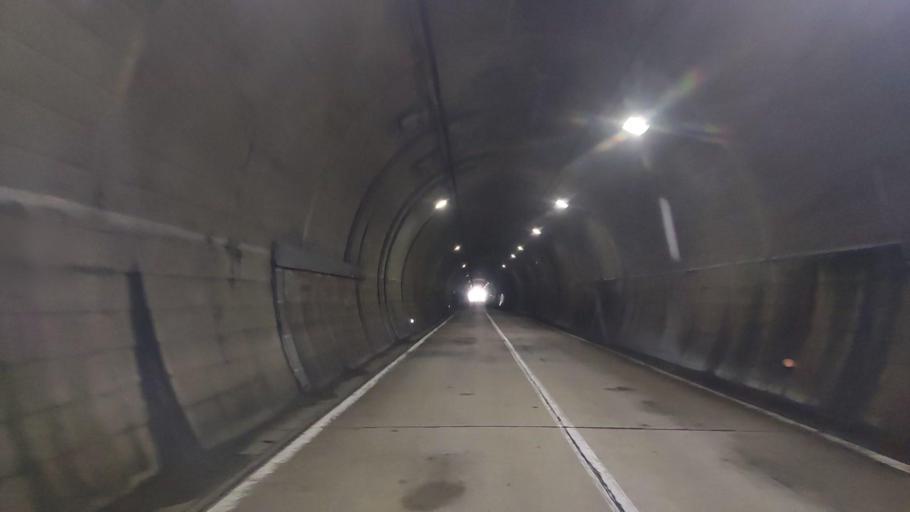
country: JP
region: Fukui
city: Ono
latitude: 35.9213
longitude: 136.5415
